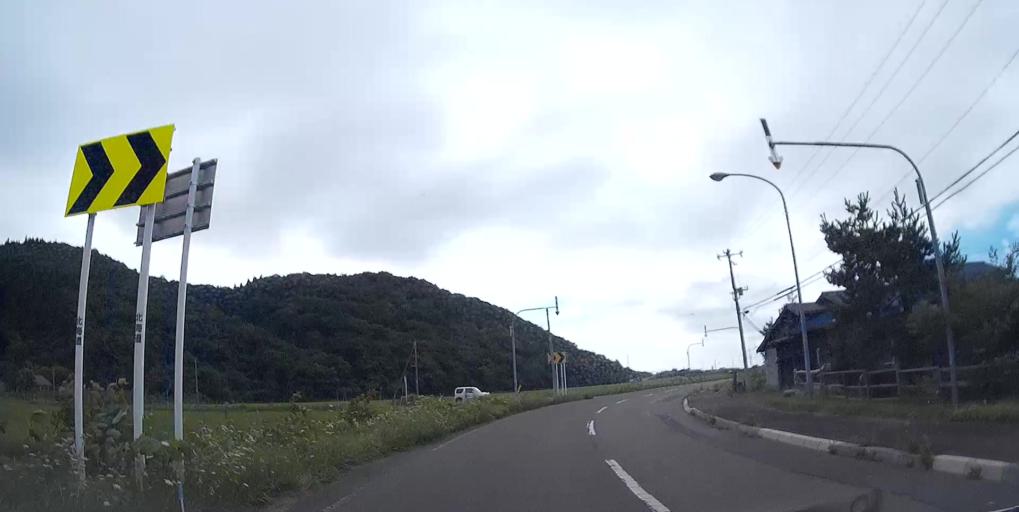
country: JP
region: Hokkaido
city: Kamiiso
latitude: 41.9722
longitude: 140.1556
